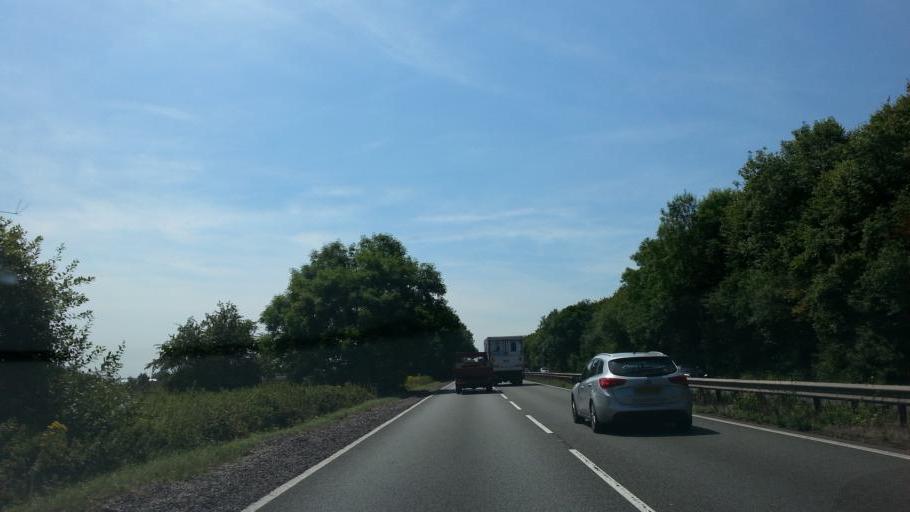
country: GB
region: England
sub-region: Staffordshire
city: Burton upon Trent
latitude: 52.8114
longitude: -1.6593
